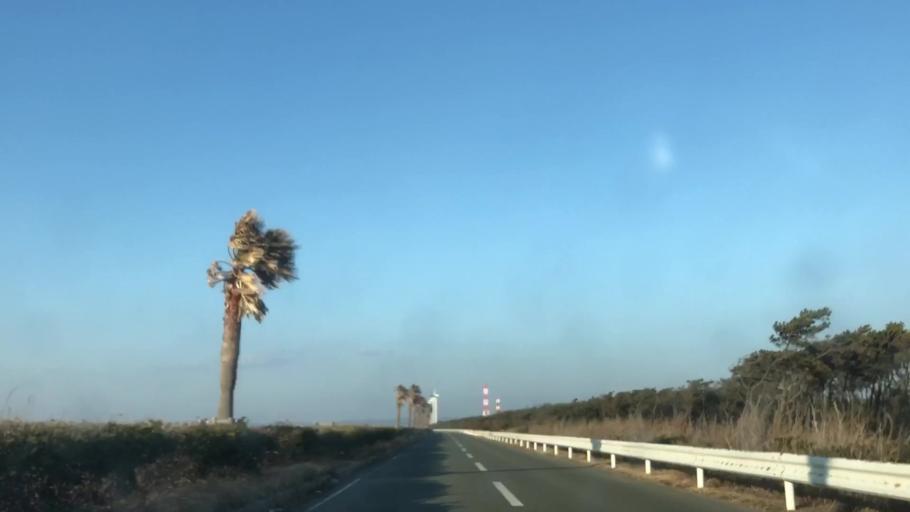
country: JP
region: Aichi
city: Toyohama
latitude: 34.6230
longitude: 137.0440
